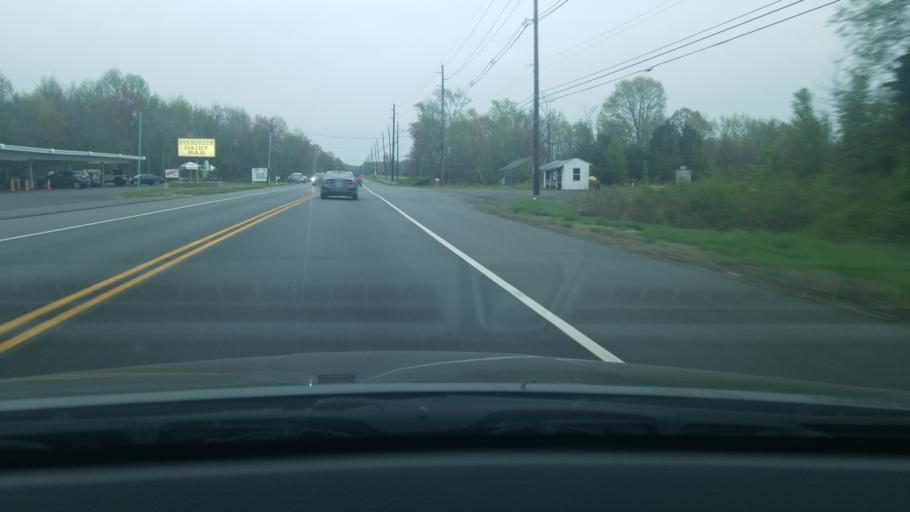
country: US
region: New Jersey
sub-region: Burlington County
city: Medford Lakes
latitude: 39.8960
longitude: -74.7809
